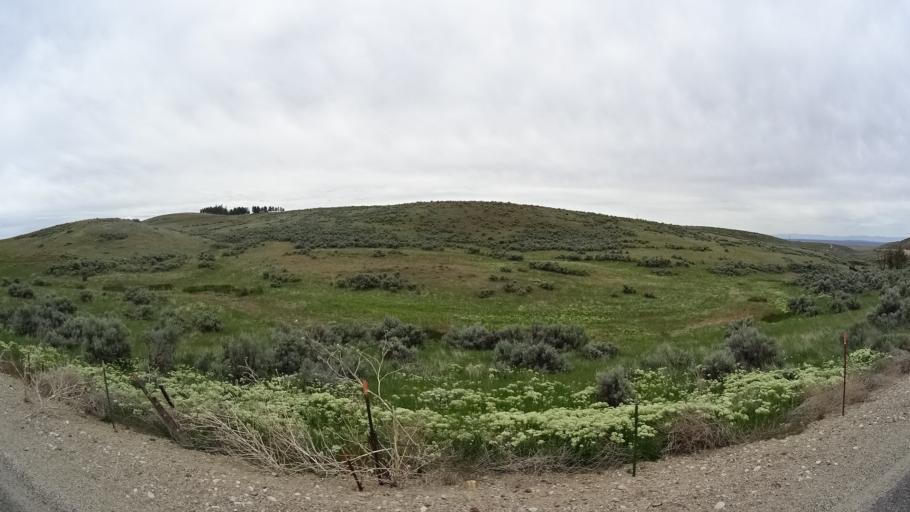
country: US
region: Idaho
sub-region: Ada County
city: Boise
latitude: 43.4888
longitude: -116.0146
